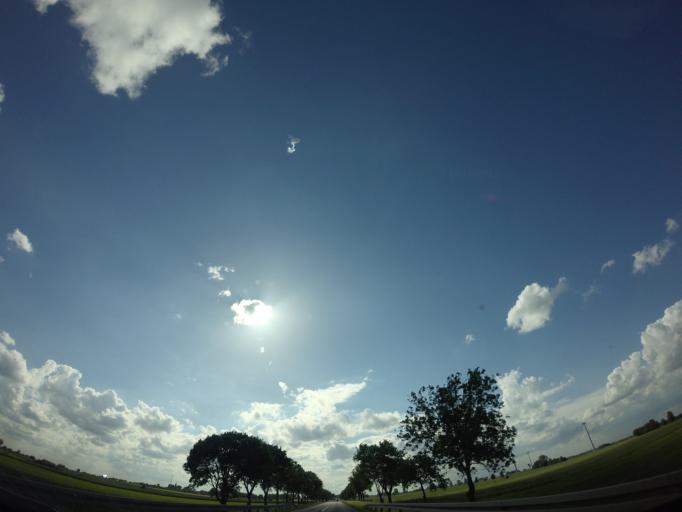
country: PL
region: West Pomeranian Voivodeship
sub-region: Powiat stargardzki
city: Suchan
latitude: 53.2819
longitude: 15.2946
